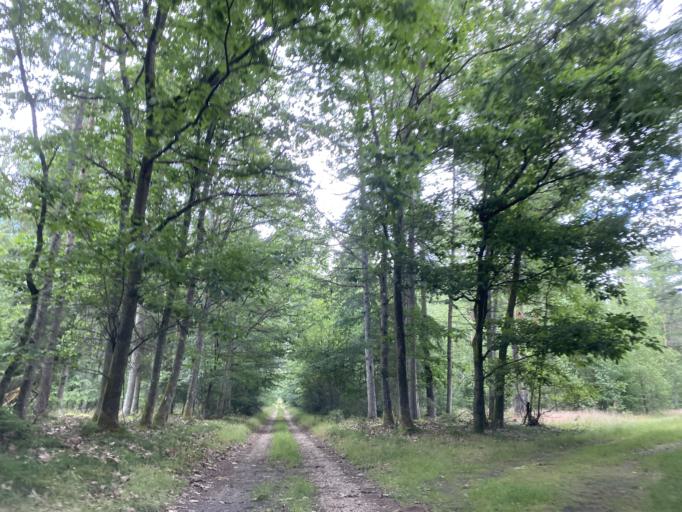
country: DK
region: Central Jutland
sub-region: Viborg Kommune
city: Bjerringbro
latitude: 56.2646
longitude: 9.6457
